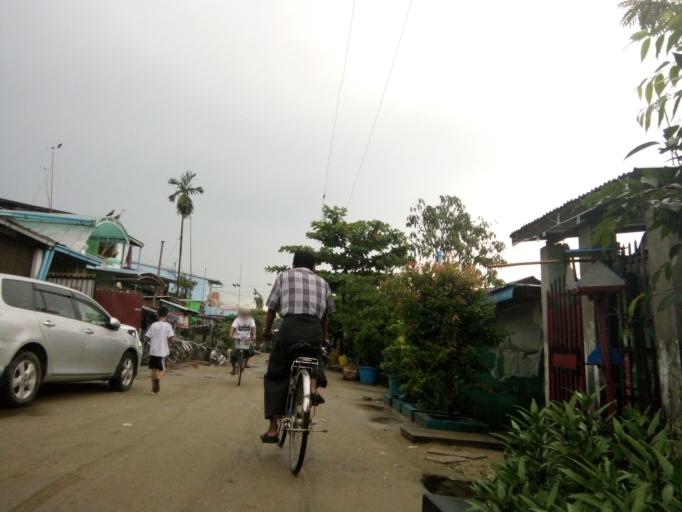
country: MM
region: Yangon
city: Yangon
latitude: 16.9134
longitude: 96.1642
